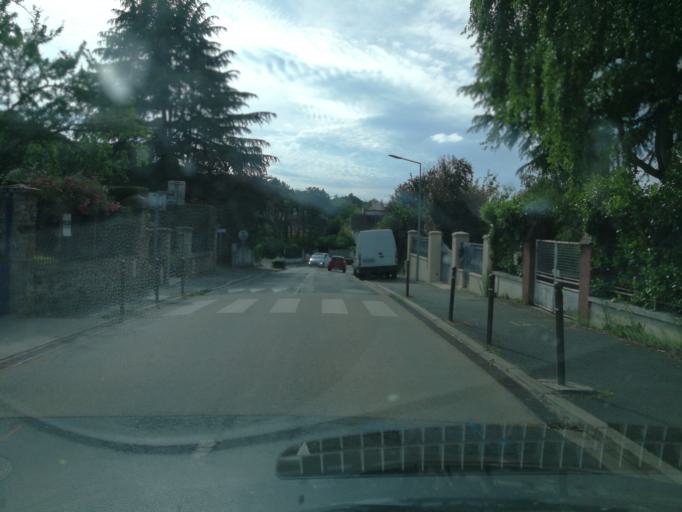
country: FR
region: Ile-de-France
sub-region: Departement des Yvelines
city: Saint-Remy-les-Chevreuse
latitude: 48.6981
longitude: 2.1032
